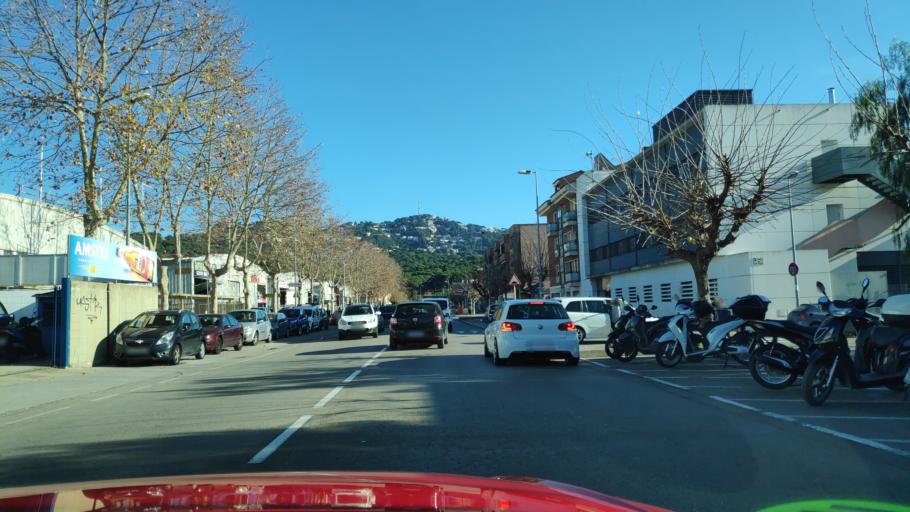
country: ES
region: Catalonia
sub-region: Provincia de Girona
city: Lloret de Mar
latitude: 41.7094
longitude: 2.8349
